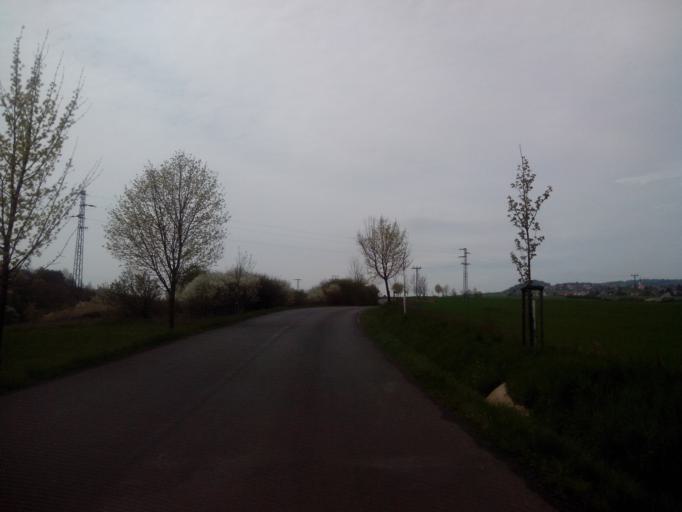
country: CZ
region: Central Bohemia
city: Hudlice
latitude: 49.9583
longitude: 13.9972
